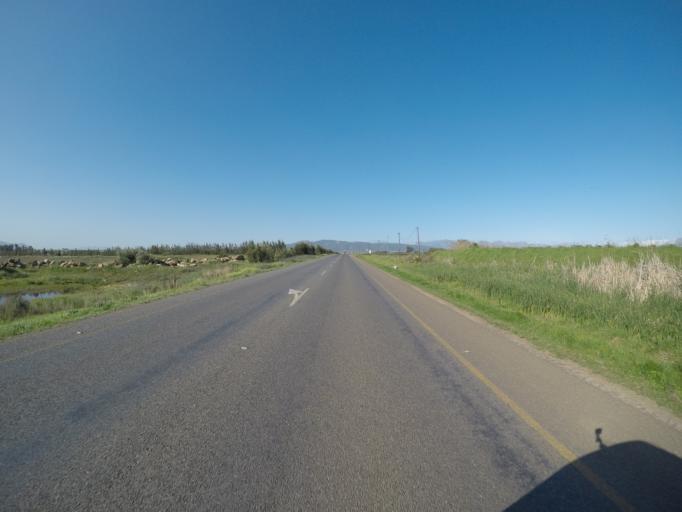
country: ZA
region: Western Cape
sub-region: City of Cape Town
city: Kraaifontein
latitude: -33.7654
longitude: 18.7918
